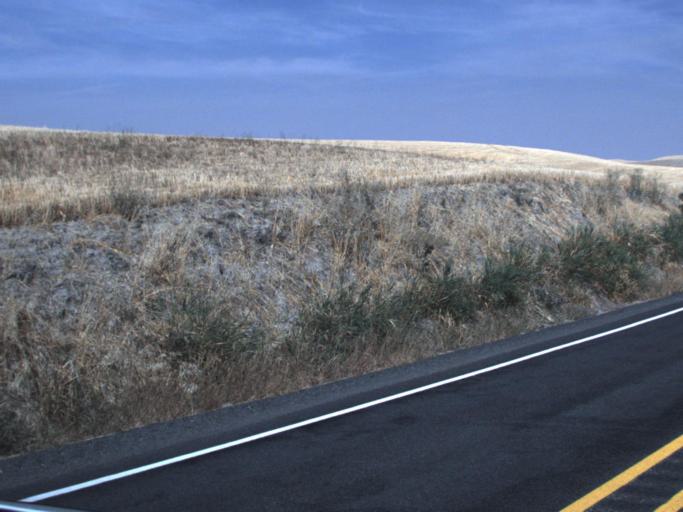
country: US
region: Idaho
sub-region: Latah County
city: Moscow
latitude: 46.9544
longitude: -117.0892
